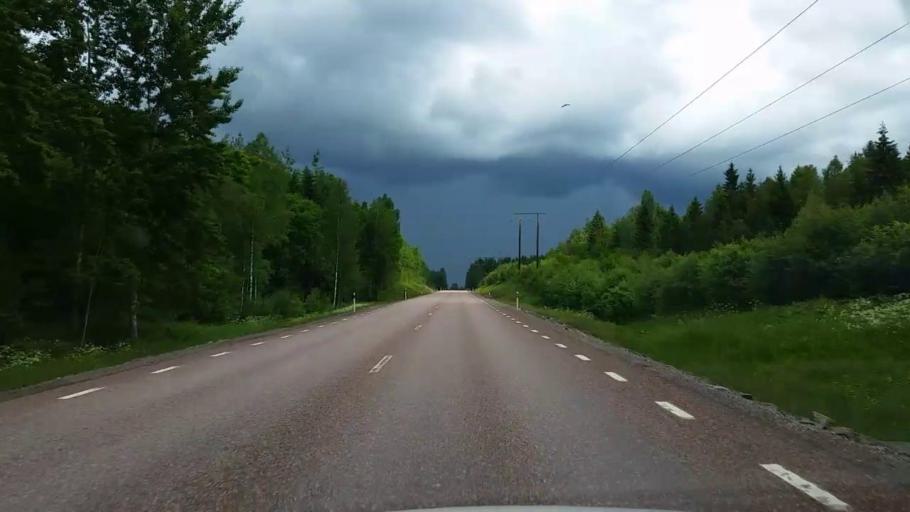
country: SE
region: Gaevleborg
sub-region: Hofors Kommun
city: Hofors
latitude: 60.5419
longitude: 16.4649
